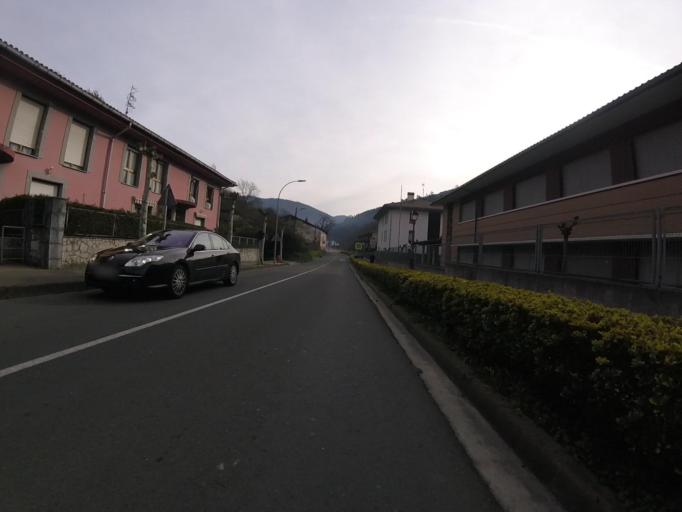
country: ES
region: Basque Country
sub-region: Provincia de Guipuzcoa
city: Berrobi
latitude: 43.1453
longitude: -2.0250
